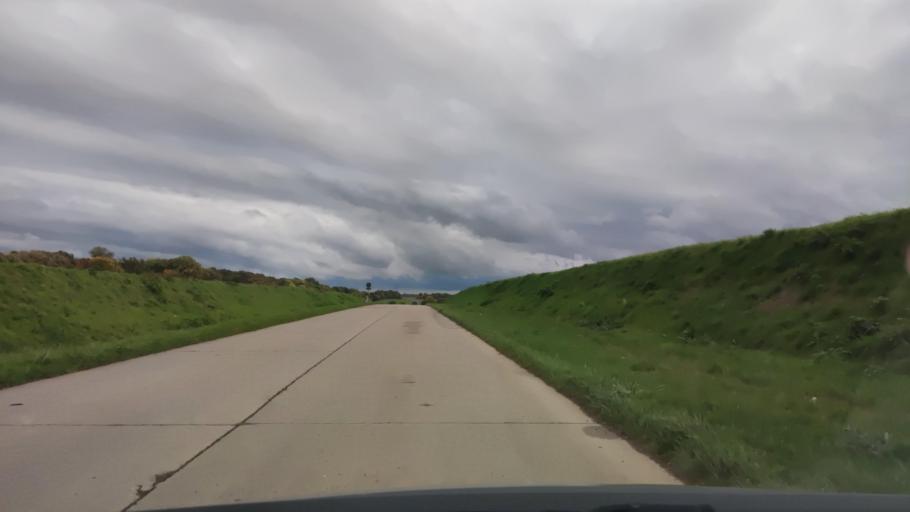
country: BE
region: Wallonia
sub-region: Province du Brabant Wallon
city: Jodoigne
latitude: 50.7123
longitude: 4.8762
